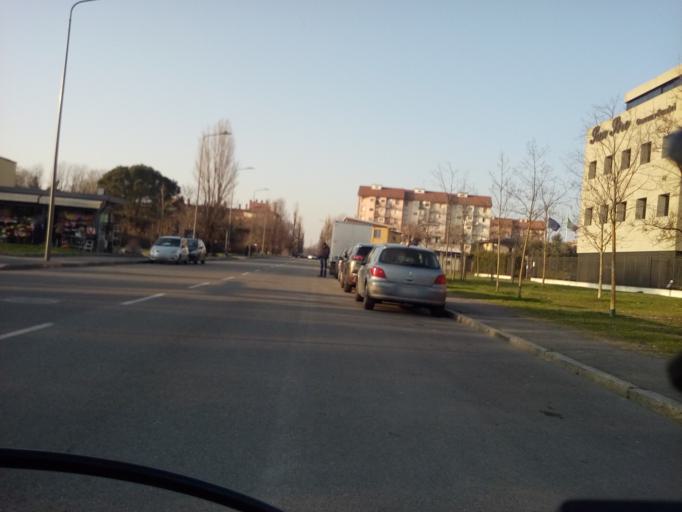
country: IT
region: Lombardy
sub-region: Citta metropolitana di Milano
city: Cesano Boscone
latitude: 45.4638
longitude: 9.0854
